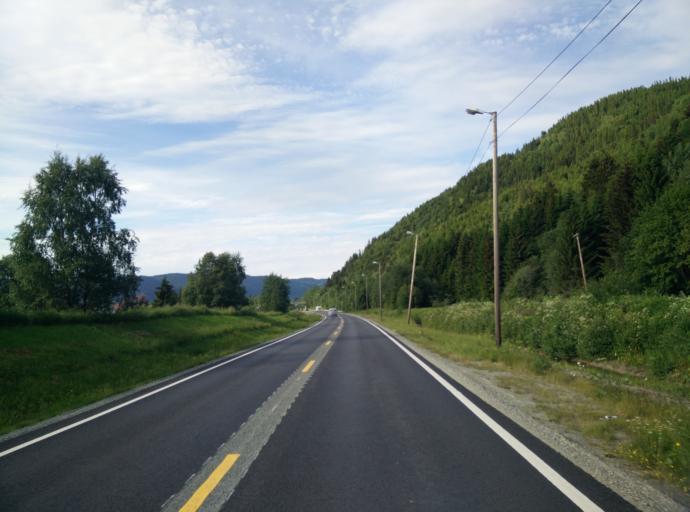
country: NO
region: Sor-Trondelag
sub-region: Orkdal
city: Orkanger
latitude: 63.2878
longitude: 9.8515
